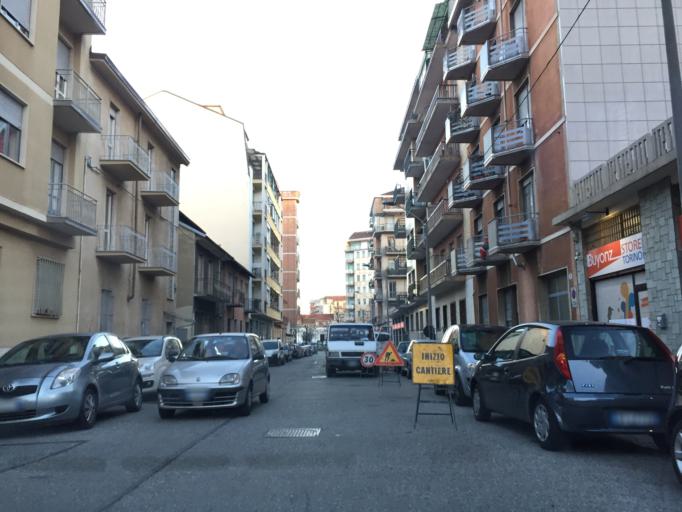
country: IT
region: Piedmont
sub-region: Provincia di Torino
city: Gerbido
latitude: 45.0391
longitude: 7.6292
